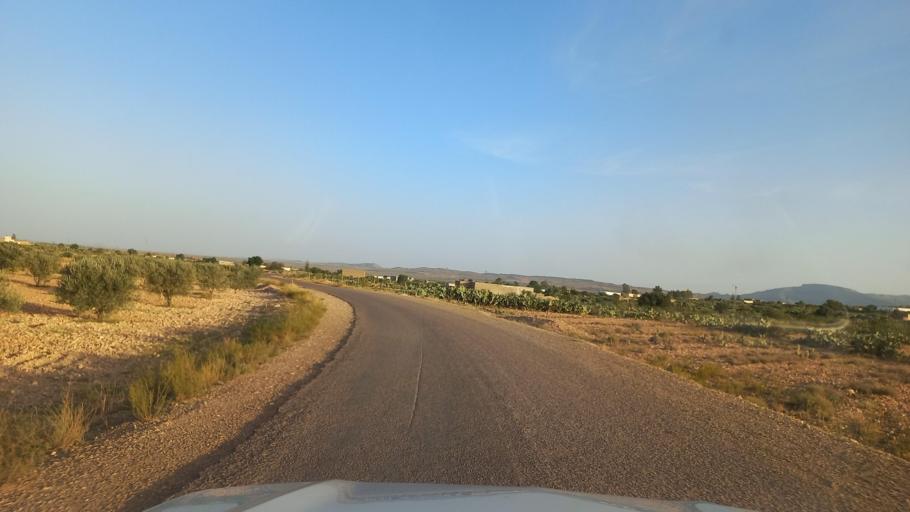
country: TN
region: Al Qasrayn
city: Kasserine
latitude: 35.2634
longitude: 8.9349
